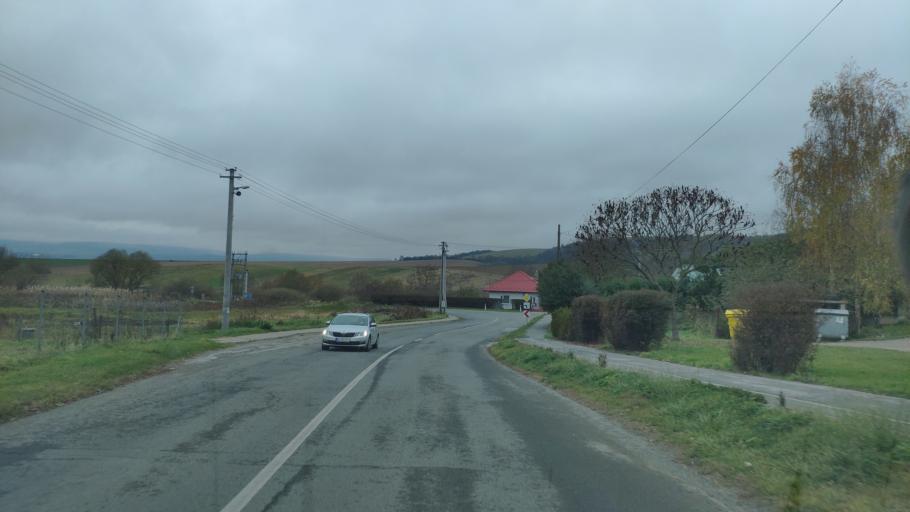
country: SK
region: Presovsky
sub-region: Okres Presov
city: Presov
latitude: 49.0690
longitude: 21.2036
